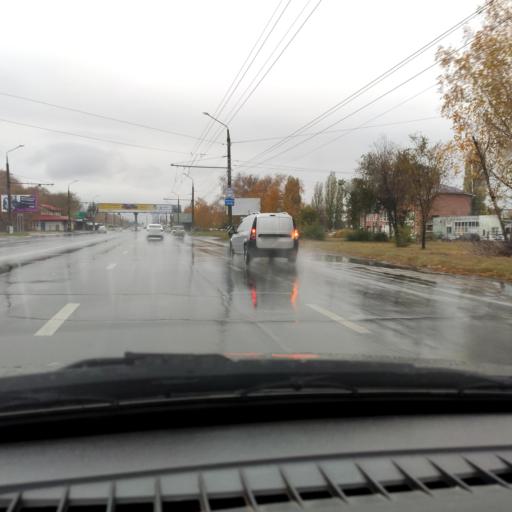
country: RU
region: Samara
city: Tol'yatti
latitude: 53.5515
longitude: 49.3094
